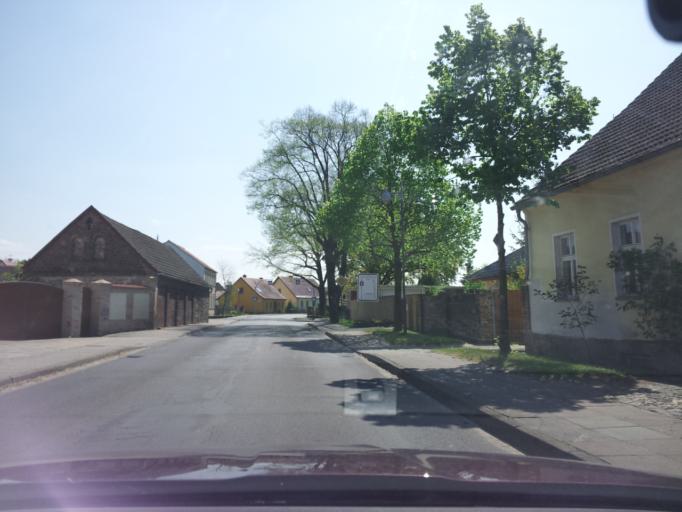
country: DE
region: Brandenburg
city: Michendorf
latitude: 52.3183
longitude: 13.1275
